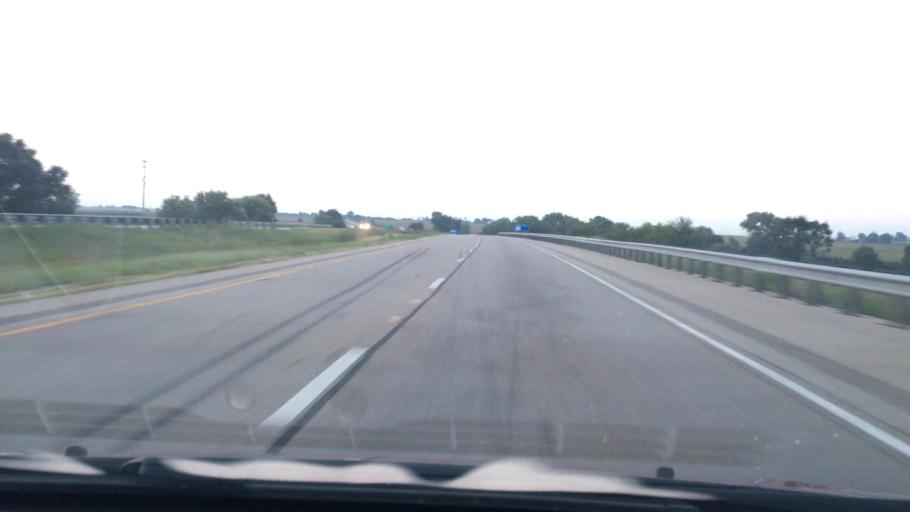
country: US
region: Illinois
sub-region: Bureau County
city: Ladd
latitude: 41.3739
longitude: -89.2508
